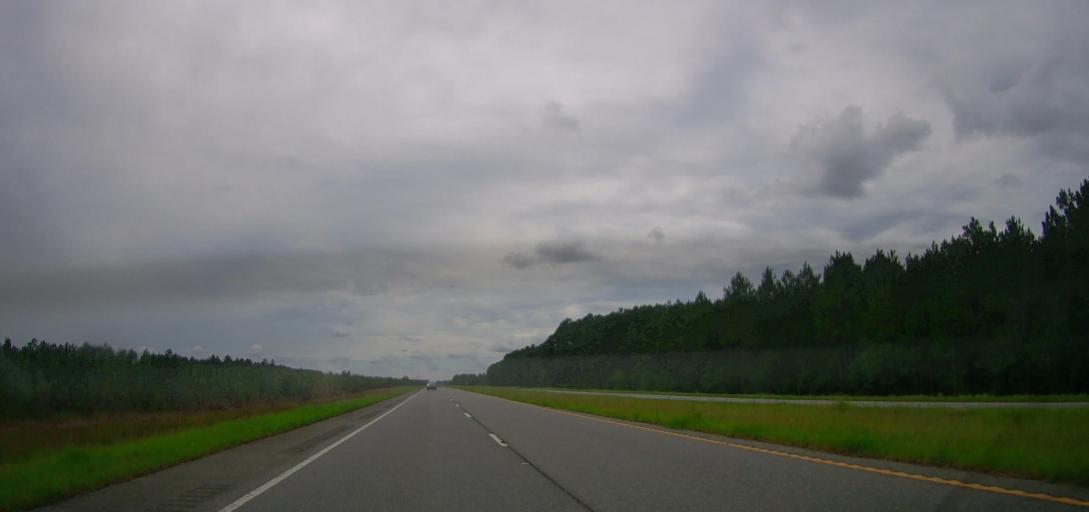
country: US
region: Georgia
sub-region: Appling County
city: Baxley
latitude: 31.7474
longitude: -82.2591
